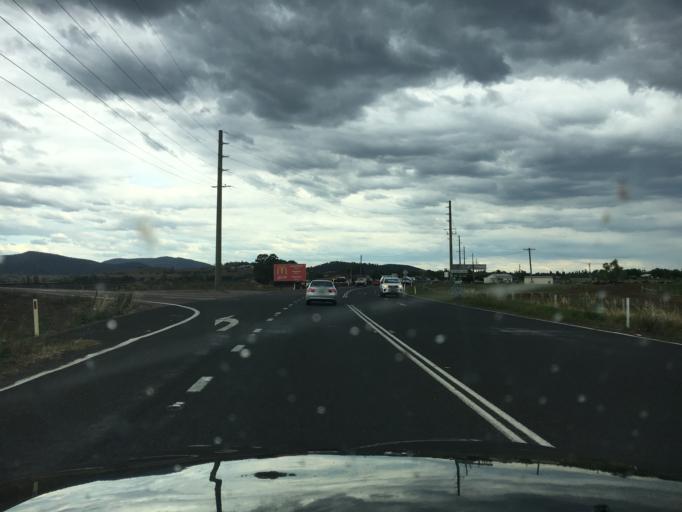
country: AU
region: New South Wales
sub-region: Muswellbrook
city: Muswellbrook
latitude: -32.1444
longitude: 150.8822
